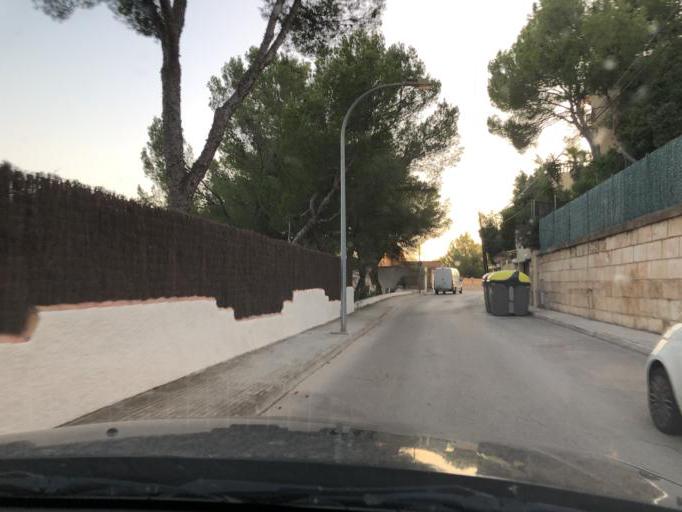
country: ES
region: Balearic Islands
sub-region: Illes Balears
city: Santa Ponsa
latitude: 39.5276
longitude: 2.4663
